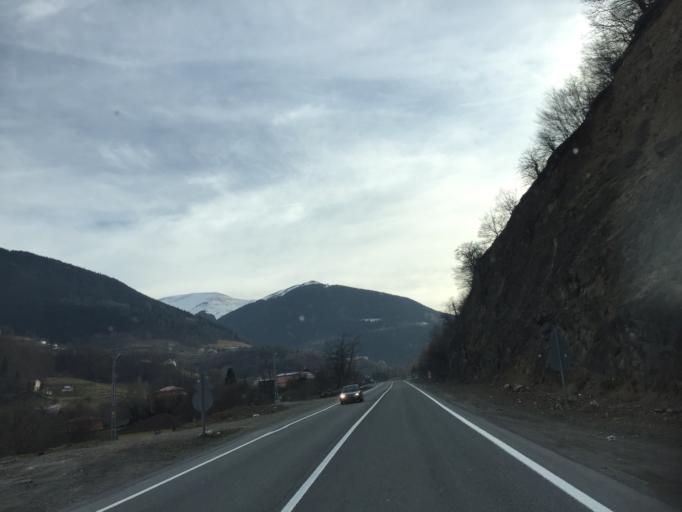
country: TR
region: Trabzon
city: Macka
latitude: 40.7222
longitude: 39.5189
